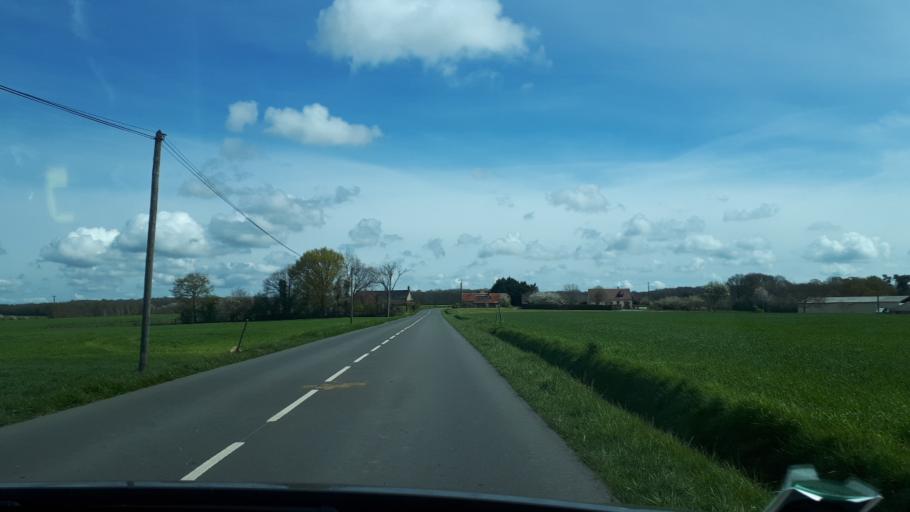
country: FR
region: Pays de la Loire
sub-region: Departement de la Sarthe
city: Le Grand-Luce
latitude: 47.8726
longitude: 0.5053
